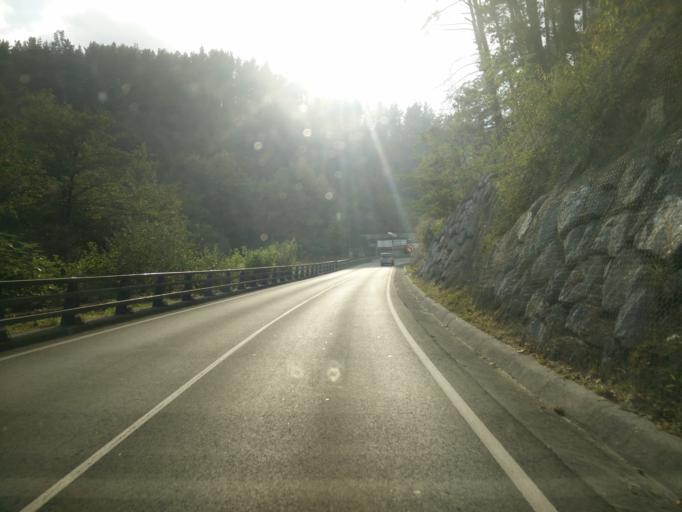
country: ES
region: Basque Country
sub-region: Bizkaia
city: Markina-Xemein
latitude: 43.2876
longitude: -2.4895
